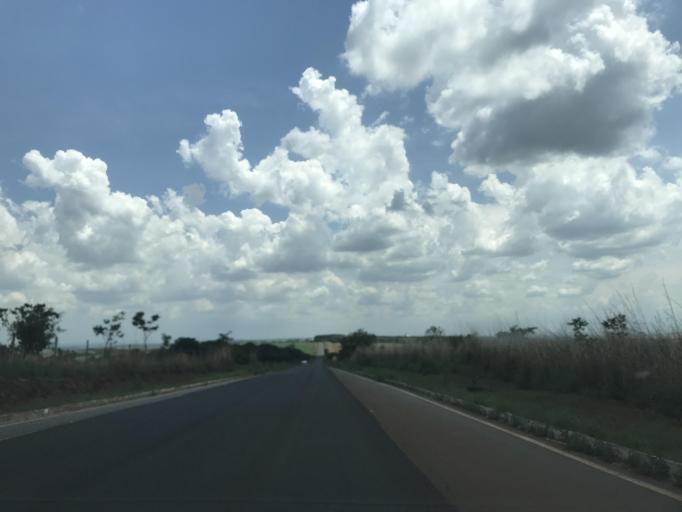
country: BR
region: Goias
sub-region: Piracanjuba
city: Piracanjuba
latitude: -17.3466
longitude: -48.7933
